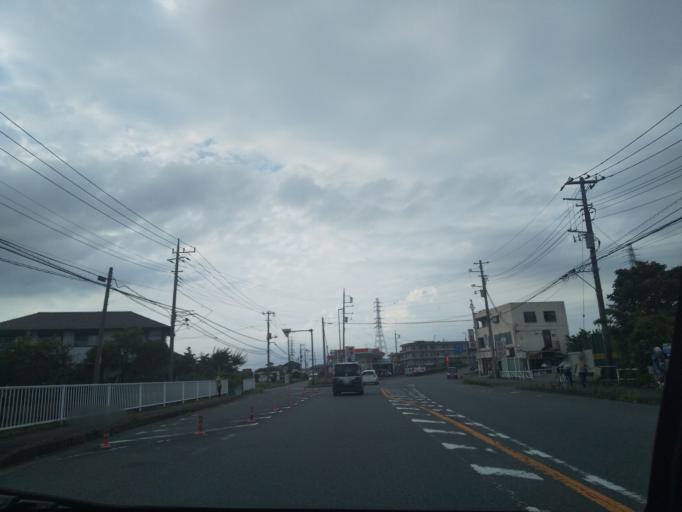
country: JP
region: Kanagawa
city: Zama
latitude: 35.4780
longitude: 139.3896
